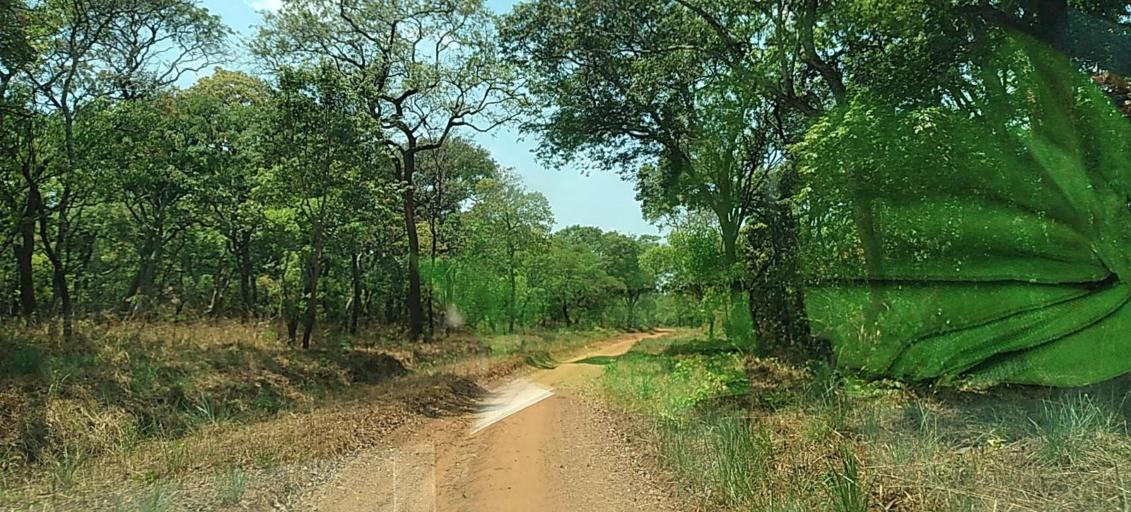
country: CD
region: Katanga
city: Kolwezi
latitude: -11.3589
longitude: 25.2065
